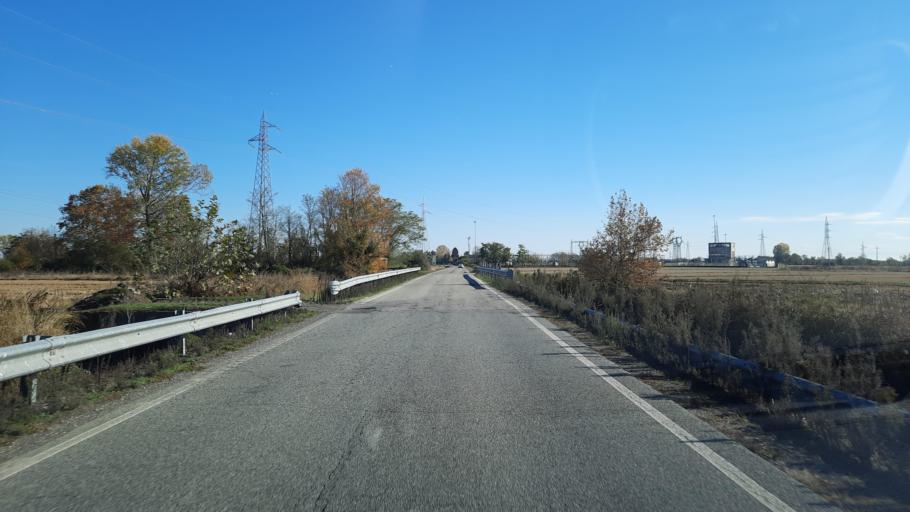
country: IT
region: Piedmont
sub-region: Provincia di Alessandria
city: Balzola
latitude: 45.1867
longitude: 8.4228
